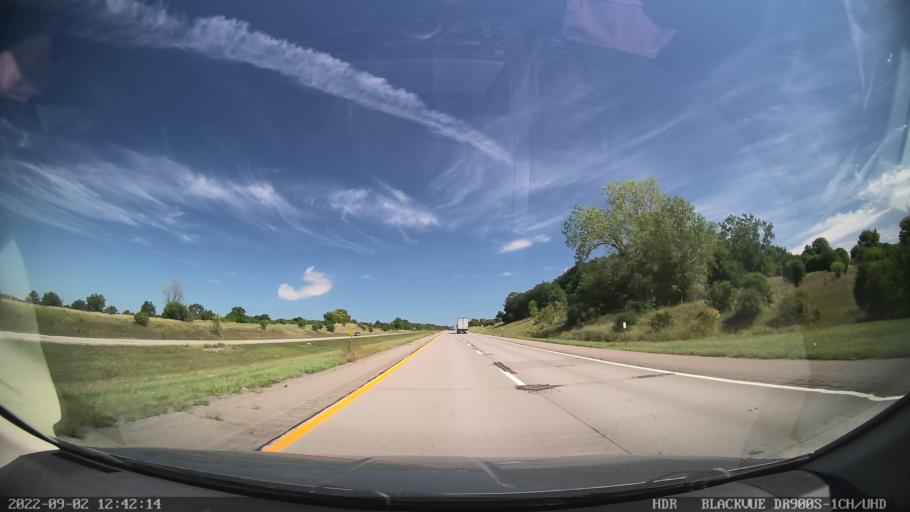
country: US
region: New York
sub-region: Livingston County
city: Geneseo
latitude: 42.7655
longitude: -77.8273
